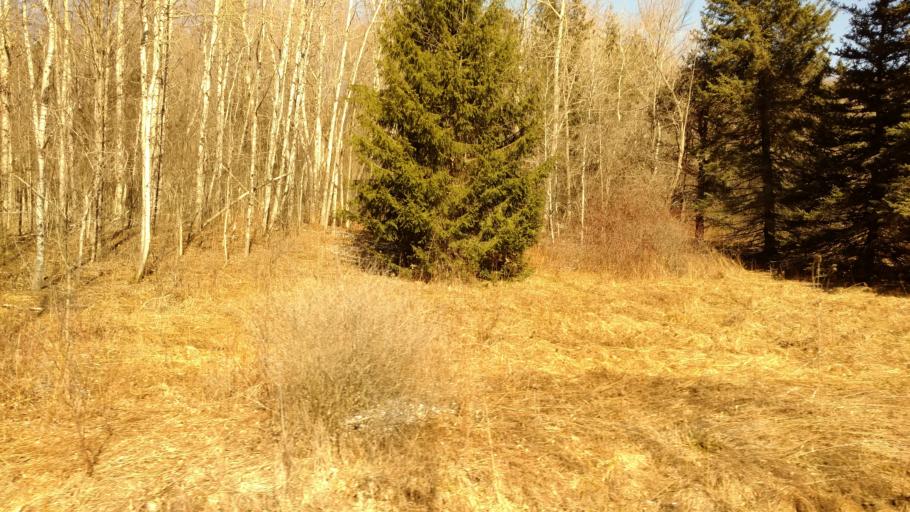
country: US
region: New York
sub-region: Allegany County
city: Wellsville
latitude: 42.0495
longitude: -77.9648
